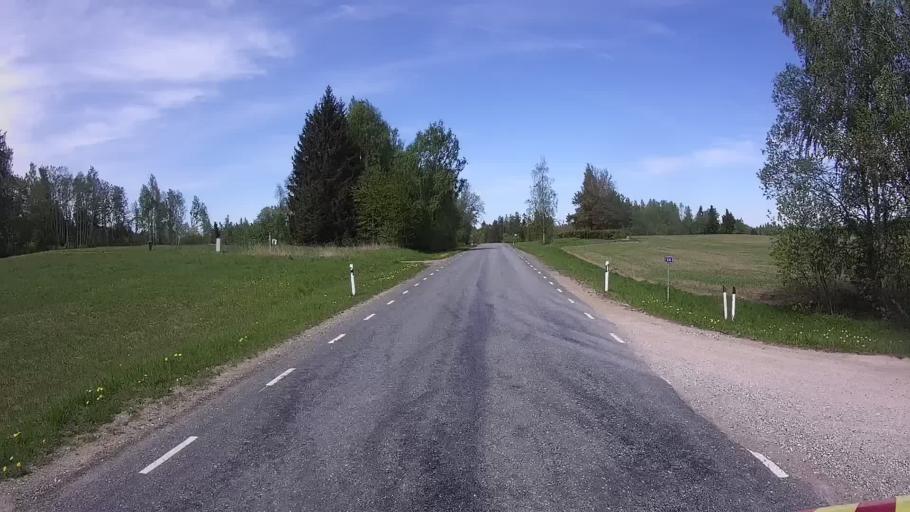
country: EE
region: Valgamaa
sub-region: Valga linn
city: Valga
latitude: 57.6877
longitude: 26.2776
